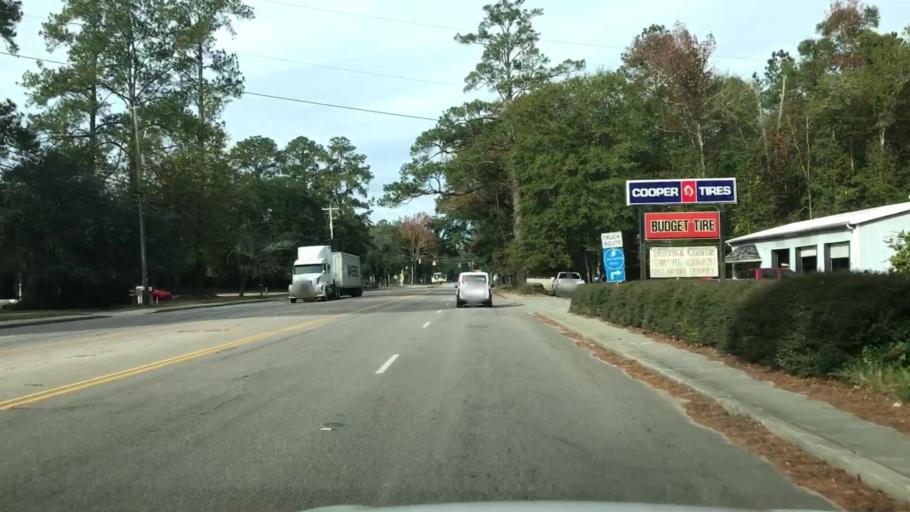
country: US
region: South Carolina
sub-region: Colleton County
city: Walterboro
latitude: 32.8971
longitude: -80.6452
